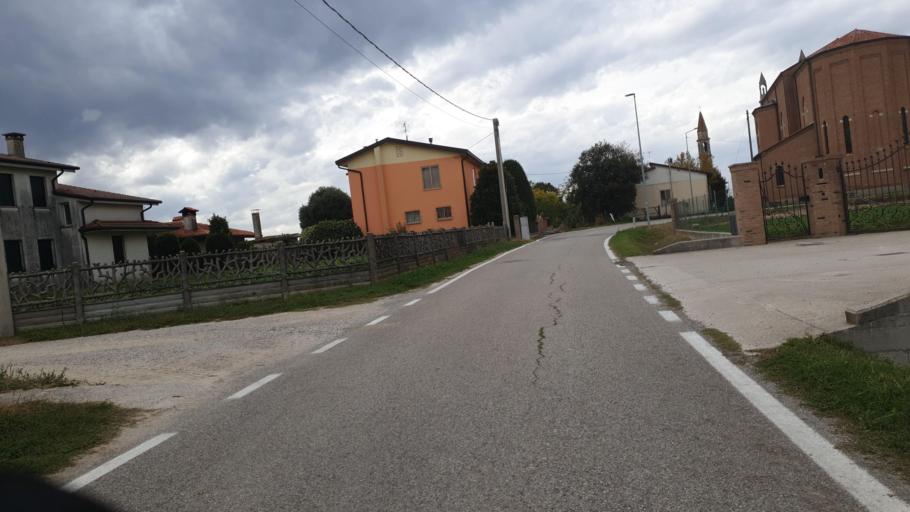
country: IT
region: Veneto
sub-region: Provincia di Padova
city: Bovolenta
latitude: 45.2745
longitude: 11.9606
